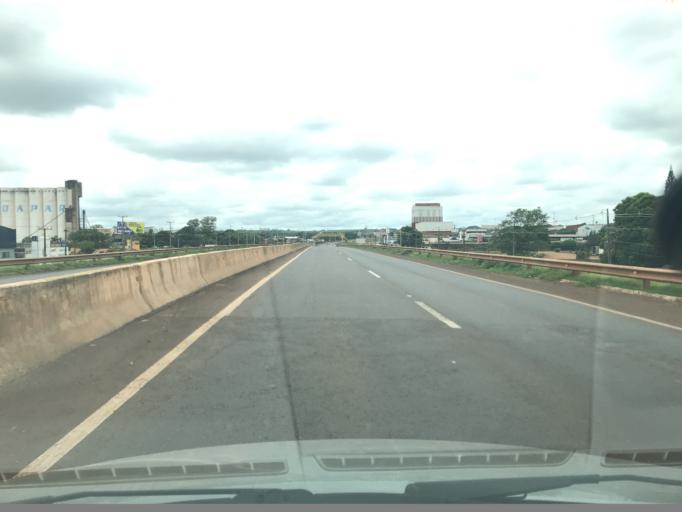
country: BR
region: Parana
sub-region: Paicandu
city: Paicandu
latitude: -23.4504
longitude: -52.0058
